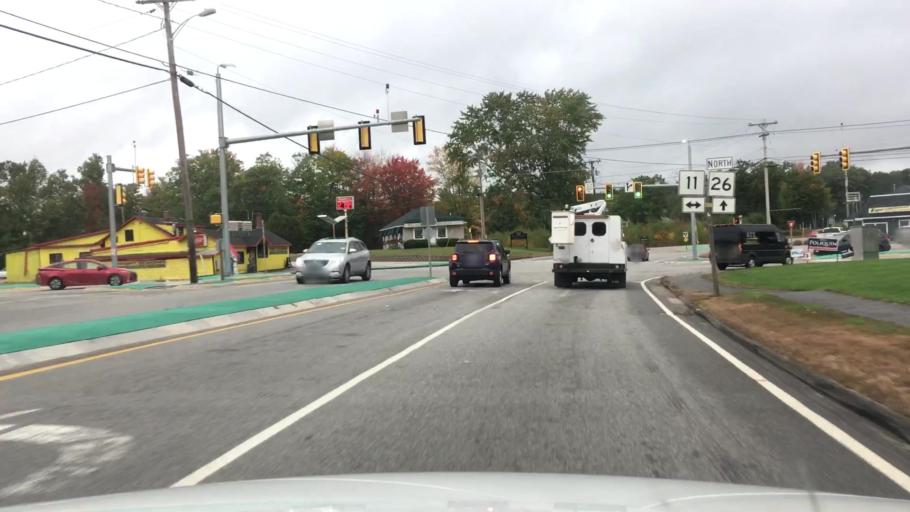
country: US
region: Maine
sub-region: Androscoggin County
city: Poland
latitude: 44.0750
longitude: -70.4160
